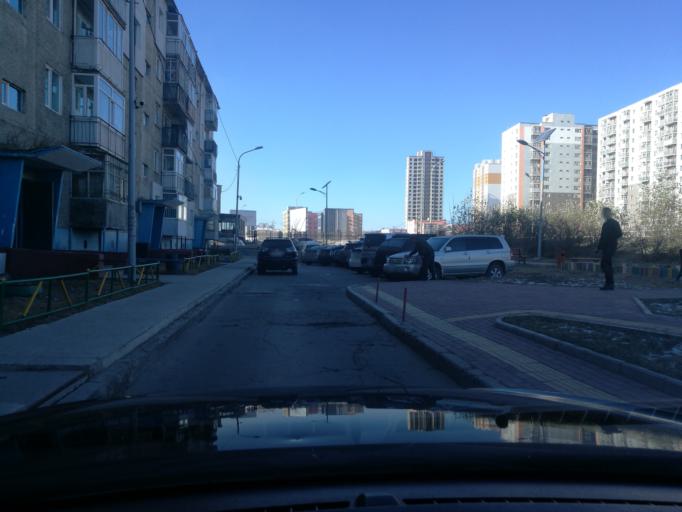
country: MN
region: Ulaanbaatar
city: Ulaanbaatar
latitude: 47.9031
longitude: 106.9026
